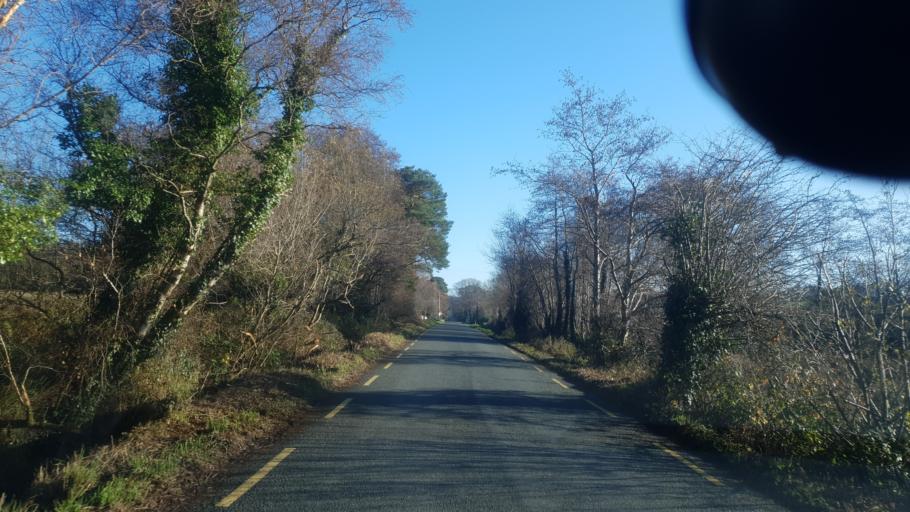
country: IE
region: Munster
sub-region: Ciarrai
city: Cill Airne
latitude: 52.1083
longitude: -9.4736
